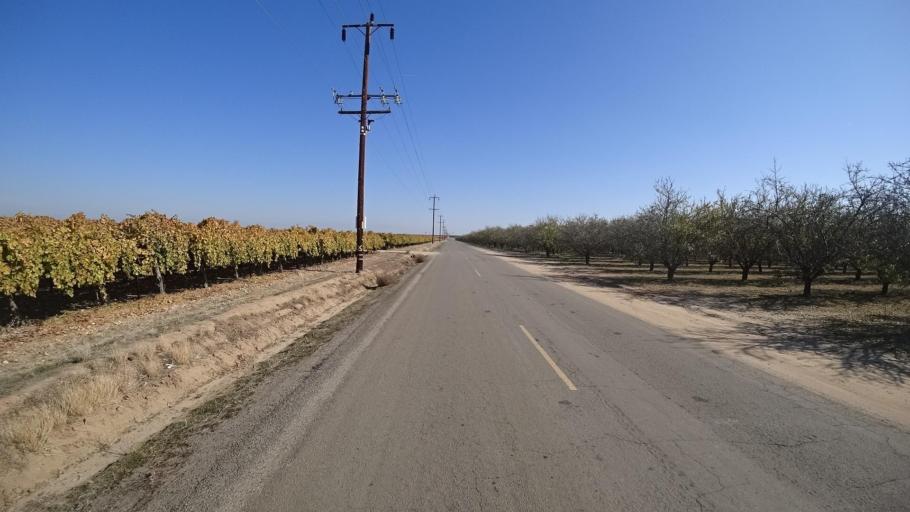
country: US
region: California
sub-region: Kern County
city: McFarland
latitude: 35.7035
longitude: -119.1497
